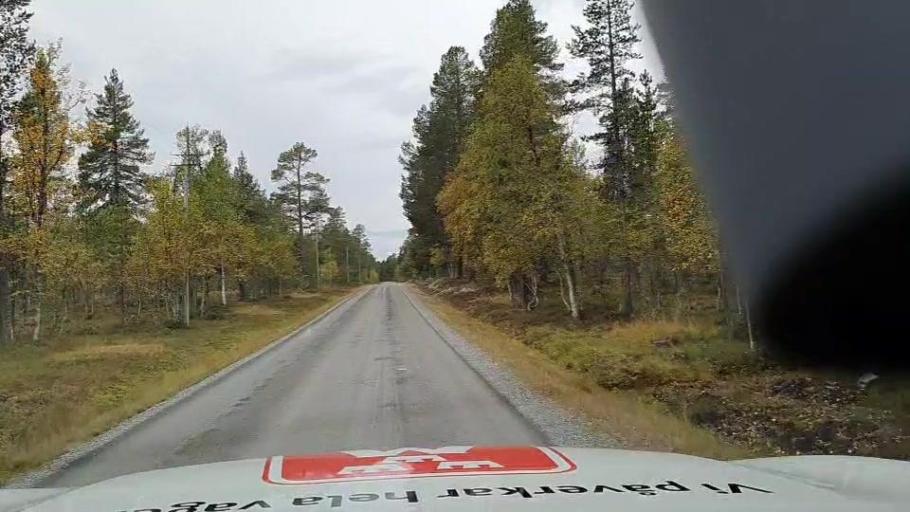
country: NO
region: Hedmark
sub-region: Engerdal
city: Engerdal
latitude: 62.0923
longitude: 12.7849
